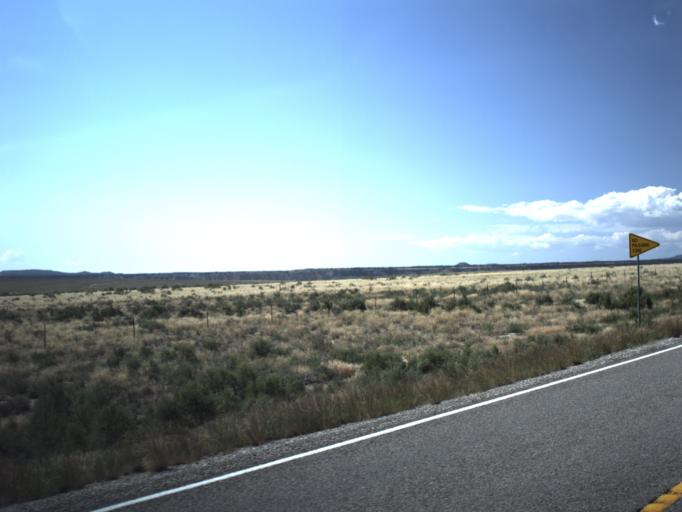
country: US
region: Utah
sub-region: Emery County
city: Ferron
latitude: 38.8419
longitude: -111.3140
